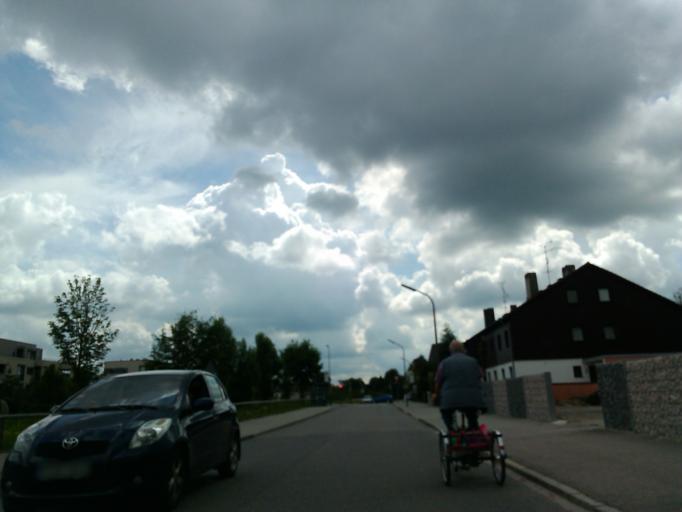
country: DE
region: Bavaria
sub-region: Upper Bavaria
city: Neubiberg
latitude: 48.1175
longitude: 11.6554
